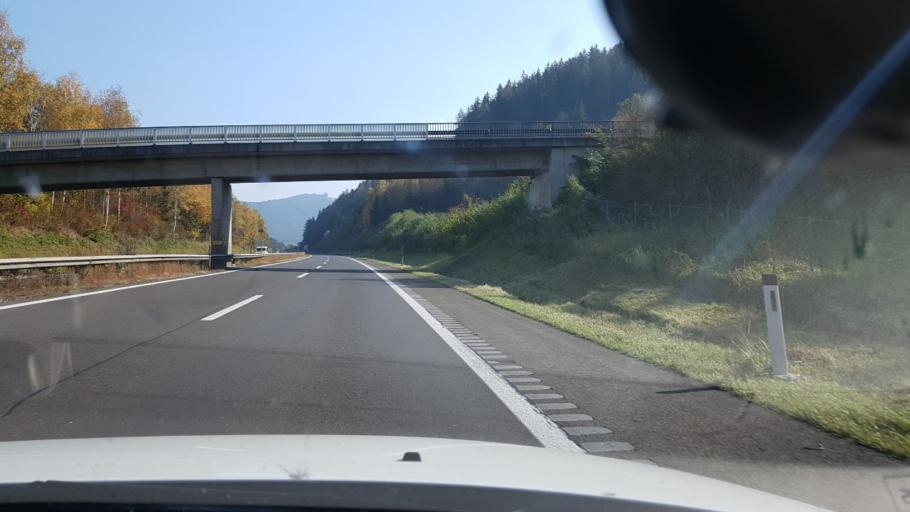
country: AT
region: Styria
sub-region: Politischer Bezirk Leoben
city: Traboch
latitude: 47.3741
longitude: 14.9648
